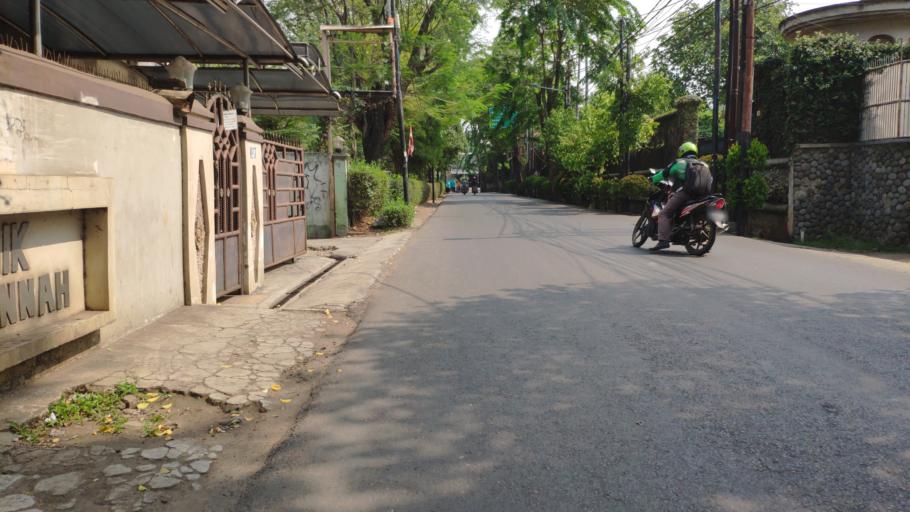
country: ID
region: Jakarta Raya
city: Jakarta
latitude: -6.2570
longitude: 106.8244
